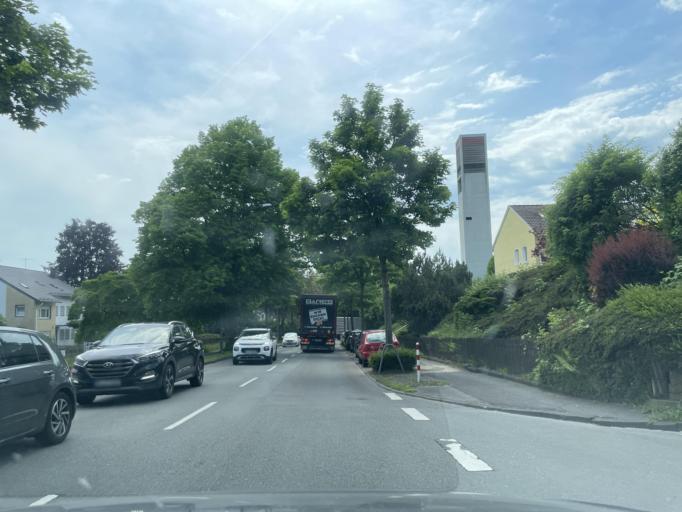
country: DE
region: North Rhine-Westphalia
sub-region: Regierungsbezirk Dusseldorf
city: Wuppertal
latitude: 51.2871
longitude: 7.1812
